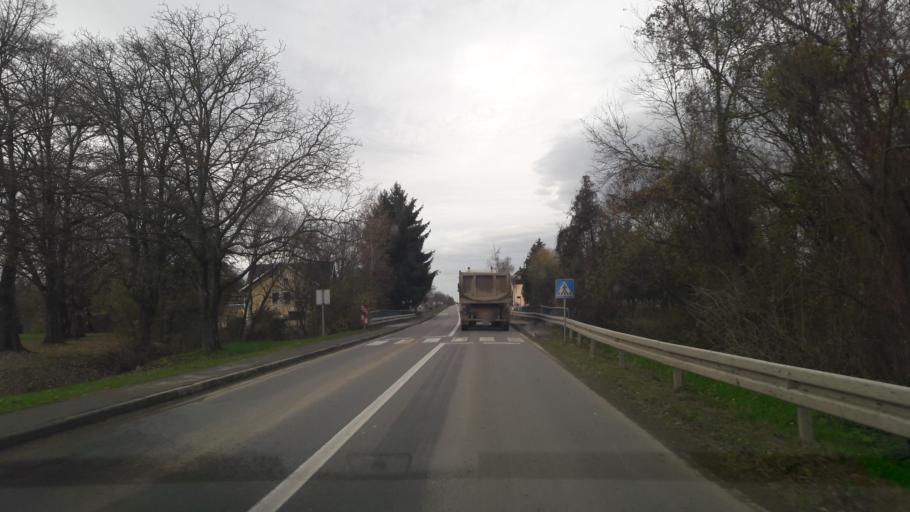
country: HR
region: Osjecko-Baranjska
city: Fericanci
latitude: 45.5246
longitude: 17.9664
